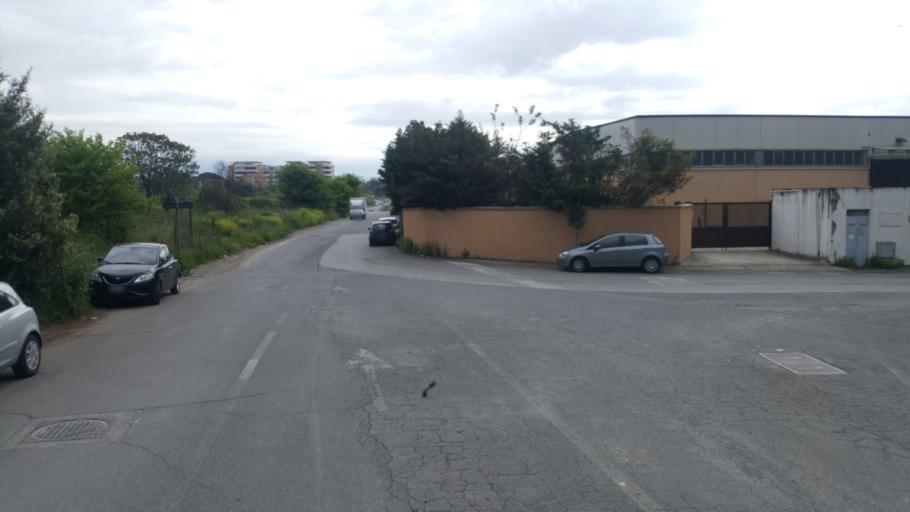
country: IT
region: Latium
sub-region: Citta metropolitana di Roma Capitale
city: Setteville
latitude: 41.9318
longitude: 12.6123
